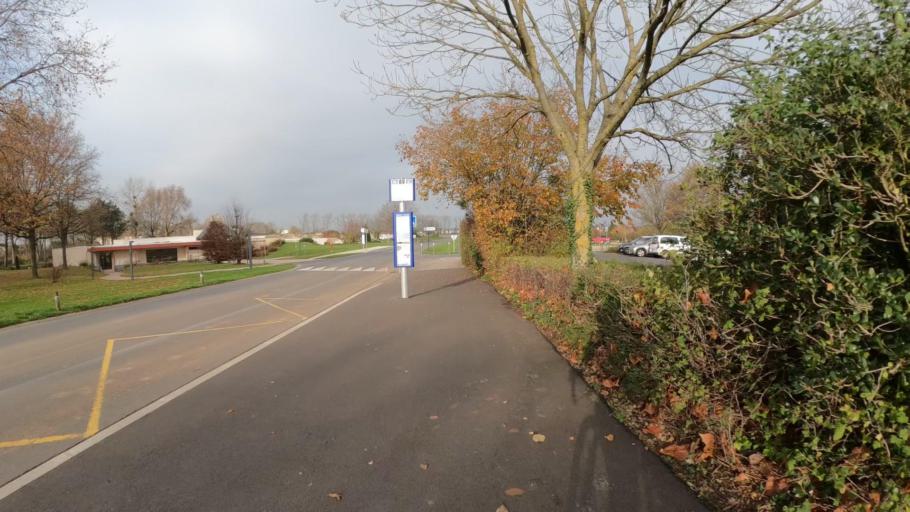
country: FR
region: Lower Normandy
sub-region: Departement du Calvados
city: Saint-Germain-la-Blanche-Herbe
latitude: 49.1941
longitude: -0.4101
